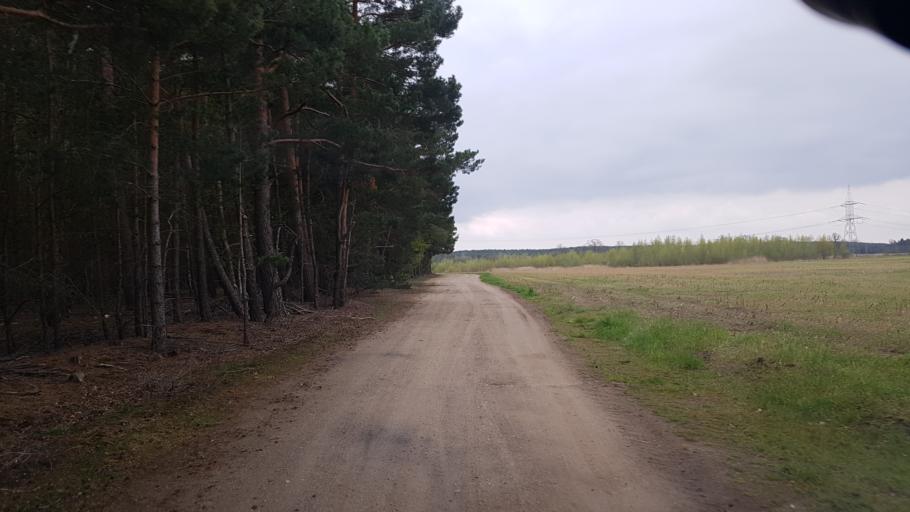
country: DE
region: Brandenburg
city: Altdobern
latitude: 51.6824
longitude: 14.0556
